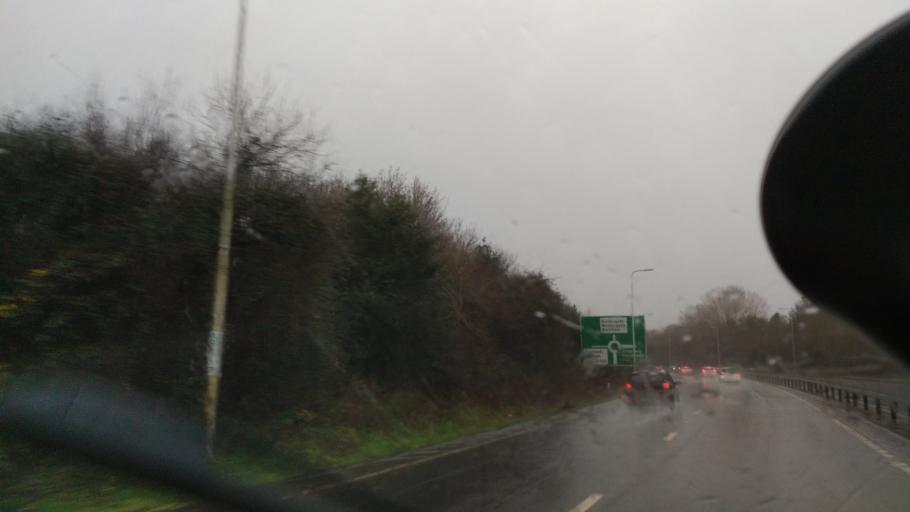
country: GB
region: England
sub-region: West Sussex
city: Fontwell
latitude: 50.8565
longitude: -0.6478
